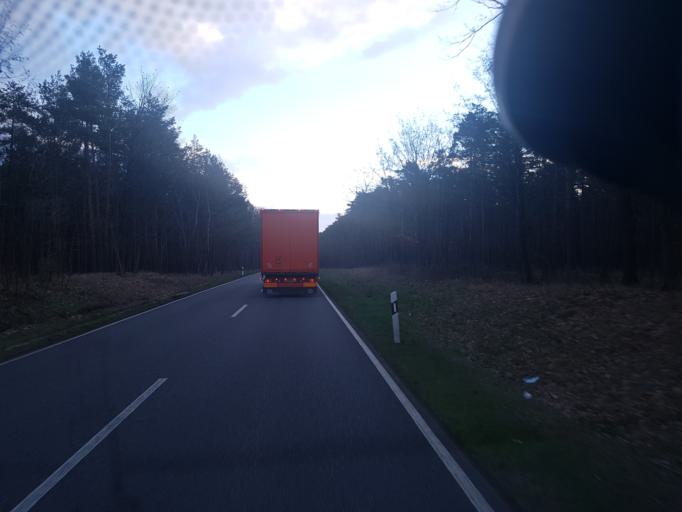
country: DE
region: Brandenburg
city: Hohenbucko
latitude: 51.7501
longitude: 13.4503
